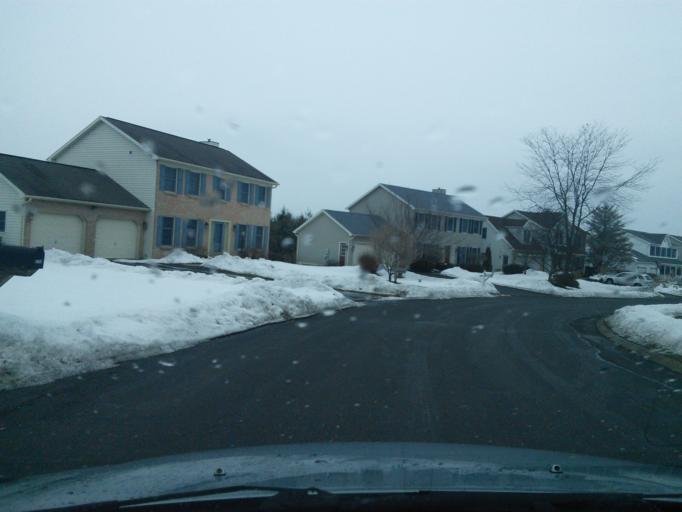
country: US
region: Pennsylvania
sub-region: Centre County
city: State College
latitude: 40.7672
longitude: -77.8769
